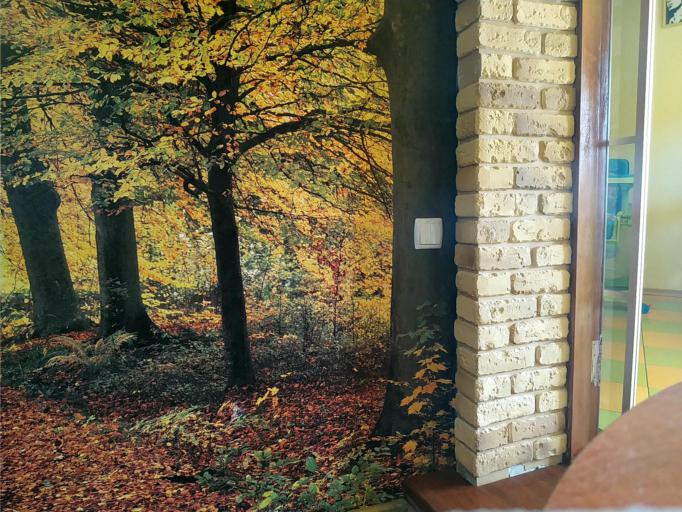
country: RU
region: Smolensk
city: Katyn'
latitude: 54.9656
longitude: 31.7271
